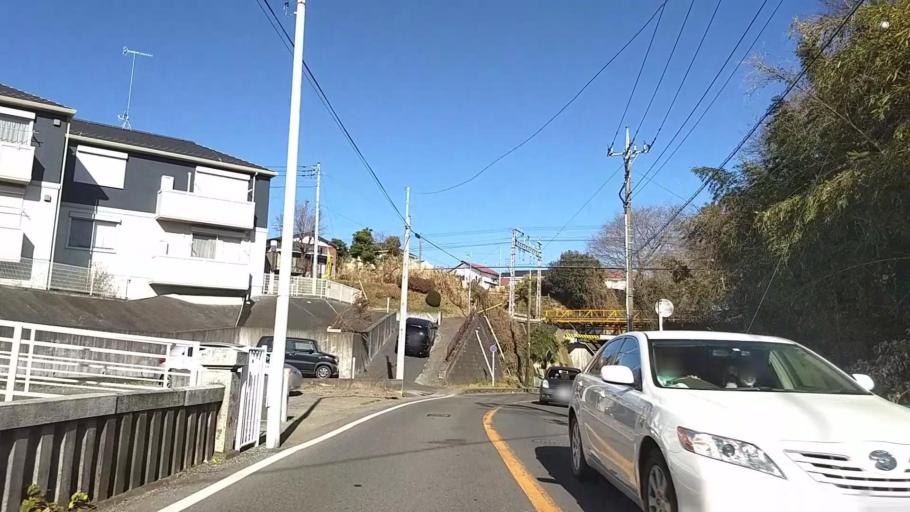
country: JP
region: Kanagawa
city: Hadano
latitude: 35.3646
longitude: 139.2327
